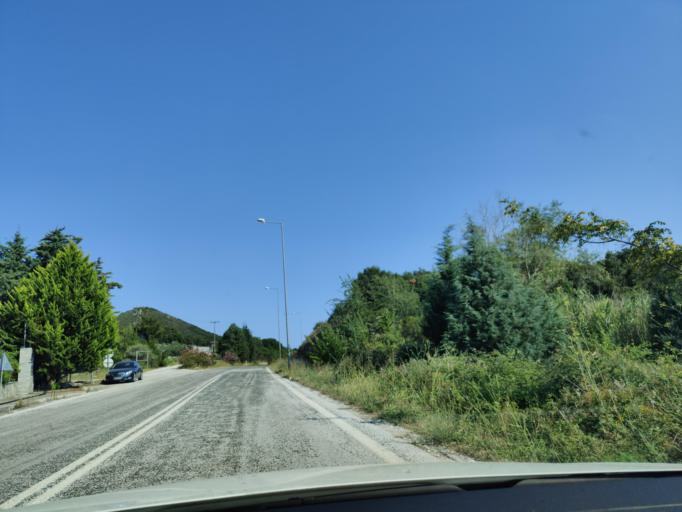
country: GR
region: East Macedonia and Thrace
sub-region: Nomos Kavalas
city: Nea Iraklitsa
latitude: 40.8651
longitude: 24.2994
